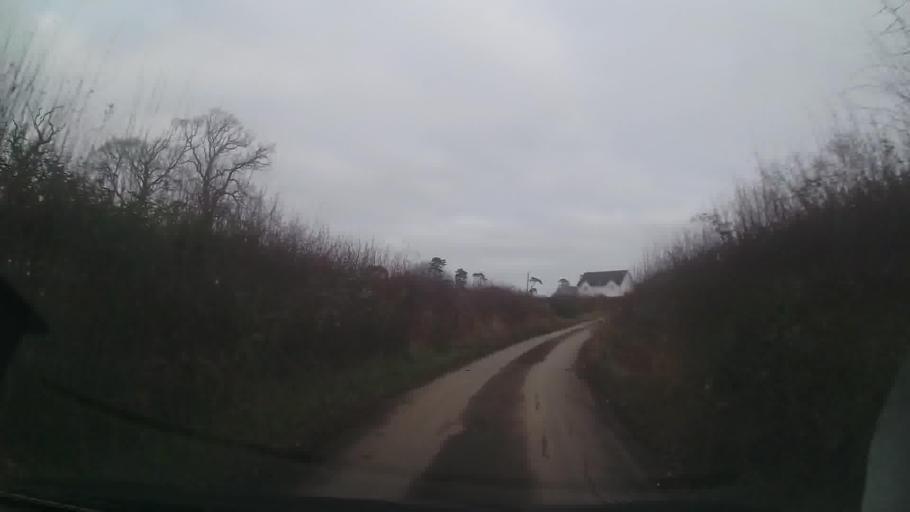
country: GB
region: England
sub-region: Shropshire
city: Petton
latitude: 52.8059
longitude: -2.8016
